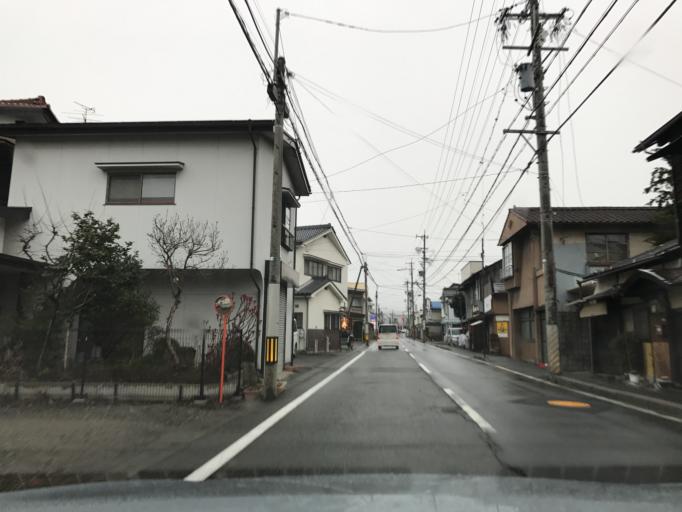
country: JP
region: Nagano
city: Matsumoto
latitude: 36.2342
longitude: 137.9604
